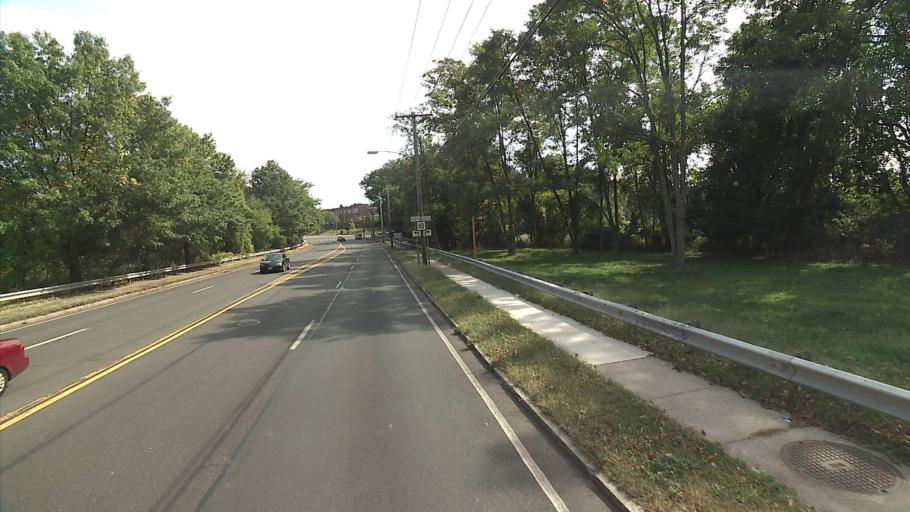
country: US
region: Connecticut
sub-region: New Haven County
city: New Haven
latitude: 41.3103
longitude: -72.9557
